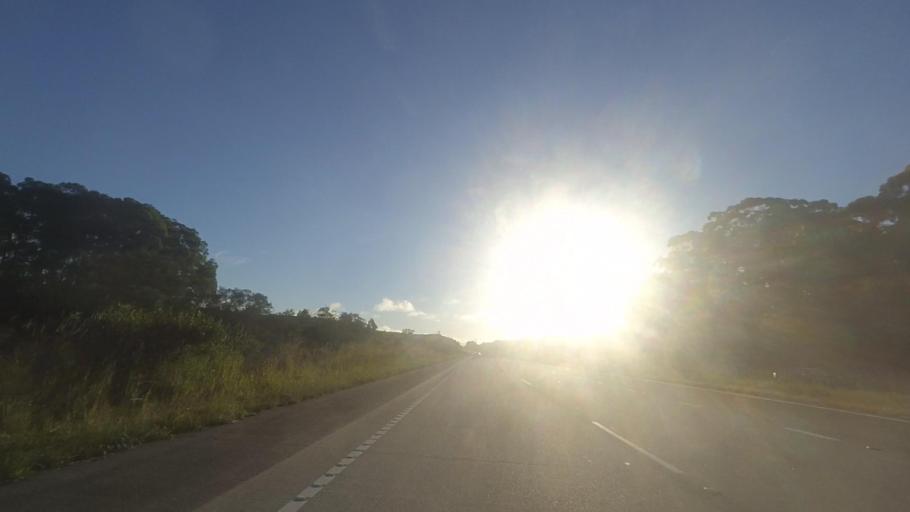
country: AU
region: New South Wales
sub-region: Great Lakes
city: Bulahdelah
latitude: -32.5267
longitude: 152.1941
